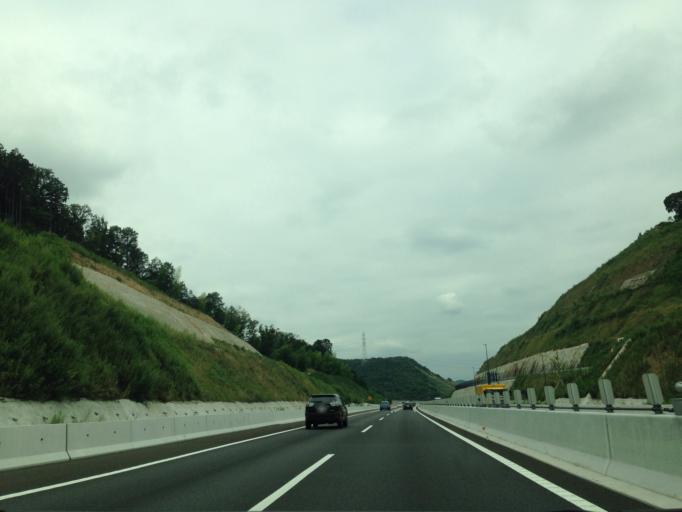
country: JP
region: Aichi
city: Gamagori
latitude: 34.9199
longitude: 137.2761
